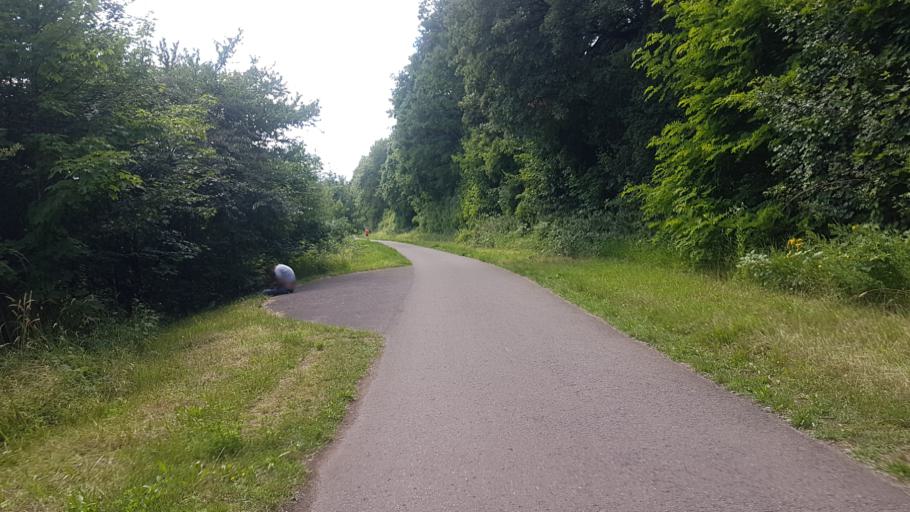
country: DE
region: Saarland
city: Volklingen
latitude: 49.2521
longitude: 6.8759
